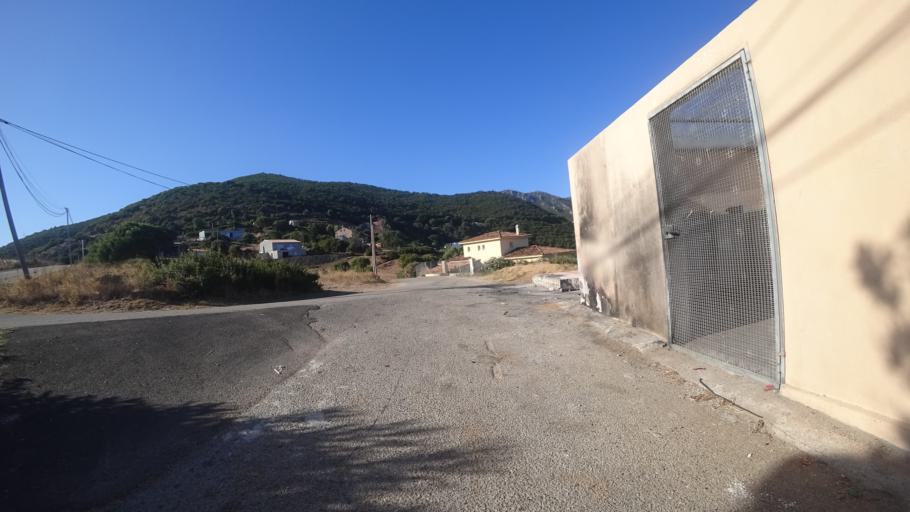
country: FR
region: Corsica
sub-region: Departement de la Corse-du-Sud
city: Alata
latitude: 41.9734
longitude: 8.6895
